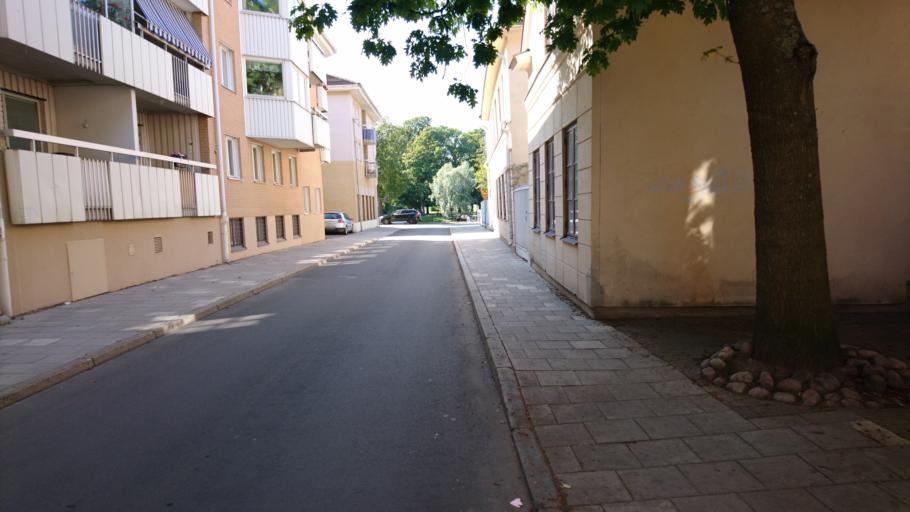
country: SE
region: Uppsala
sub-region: Uppsala Kommun
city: Uppsala
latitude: 59.8546
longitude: 17.6442
